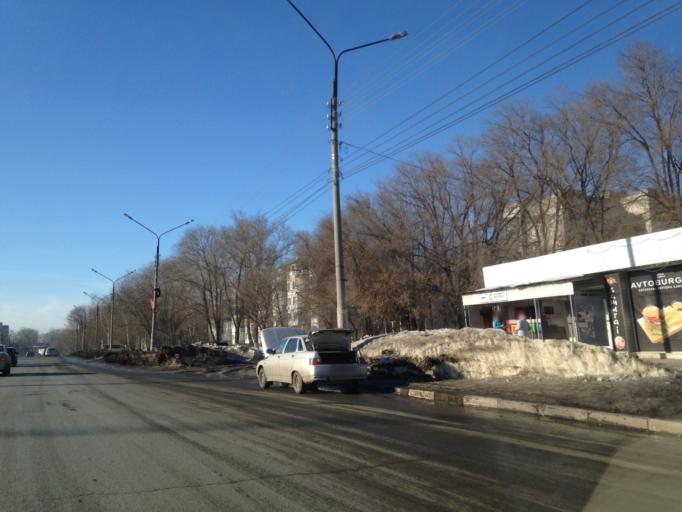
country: RU
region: Ulyanovsk
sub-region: Ulyanovskiy Rayon
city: Ulyanovsk
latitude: 54.2981
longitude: 48.3291
